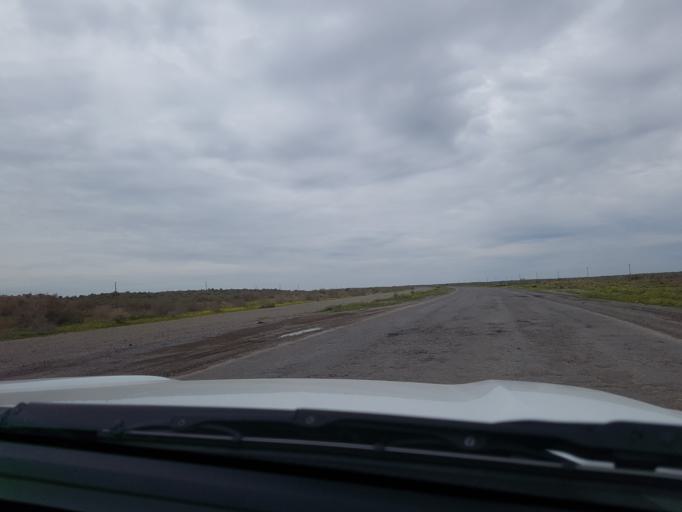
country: TM
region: Mary
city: Bayramaly
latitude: 37.9355
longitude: 62.6284
